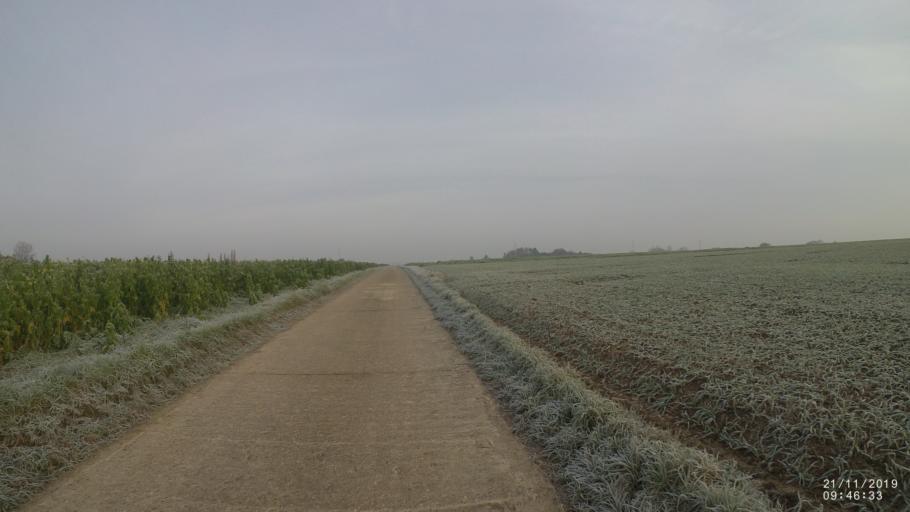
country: BE
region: Flanders
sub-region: Provincie Vlaams-Brabant
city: Tienen
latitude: 50.7927
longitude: 5.0041
